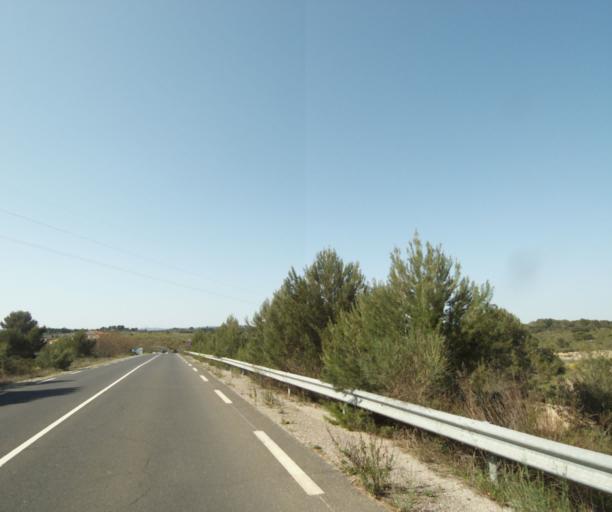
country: FR
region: Languedoc-Roussillon
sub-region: Departement de l'Herault
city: Juvignac
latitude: 43.6223
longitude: 3.7859
